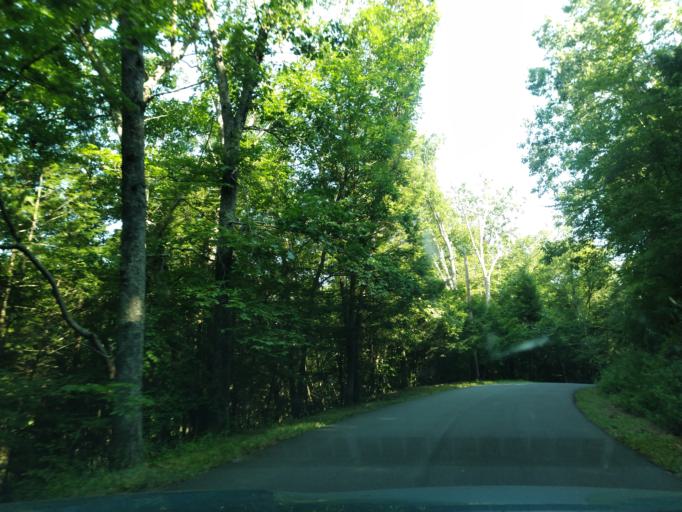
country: US
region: Connecticut
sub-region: New Haven County
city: Southbury
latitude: 41.4235
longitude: -73.2056
